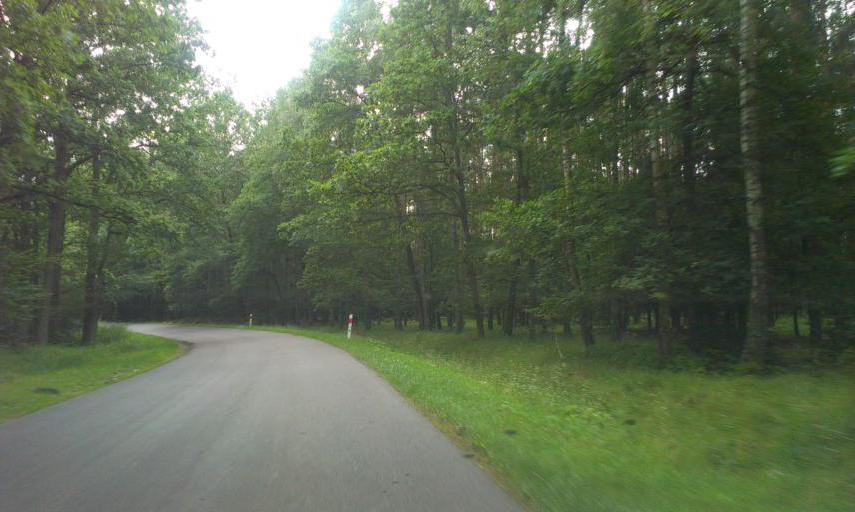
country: PL
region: West Pomeranian Voivodeship
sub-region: Powiat swidwinski
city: Polczyn-Zdroj
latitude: 53.8403
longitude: 16.1557
